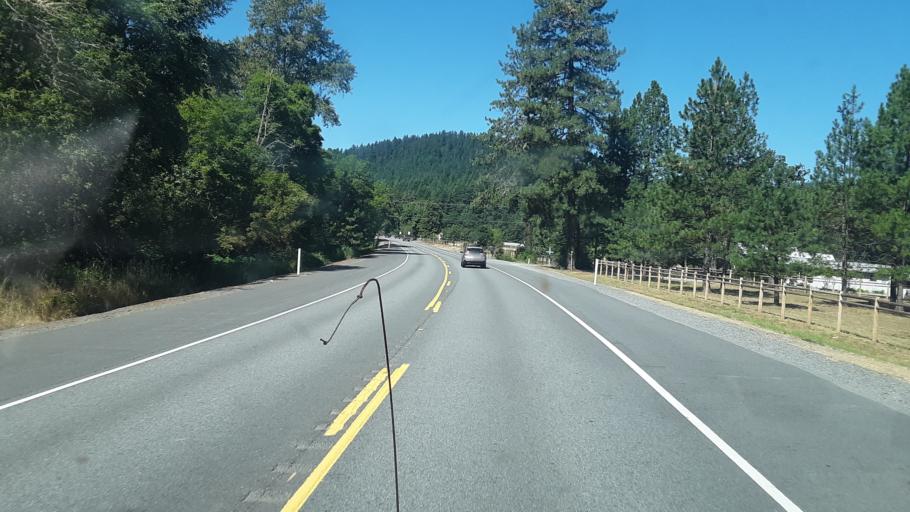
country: US
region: Oregon
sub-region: Josephine County
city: Redwood
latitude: 42.3831
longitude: -123.4831
